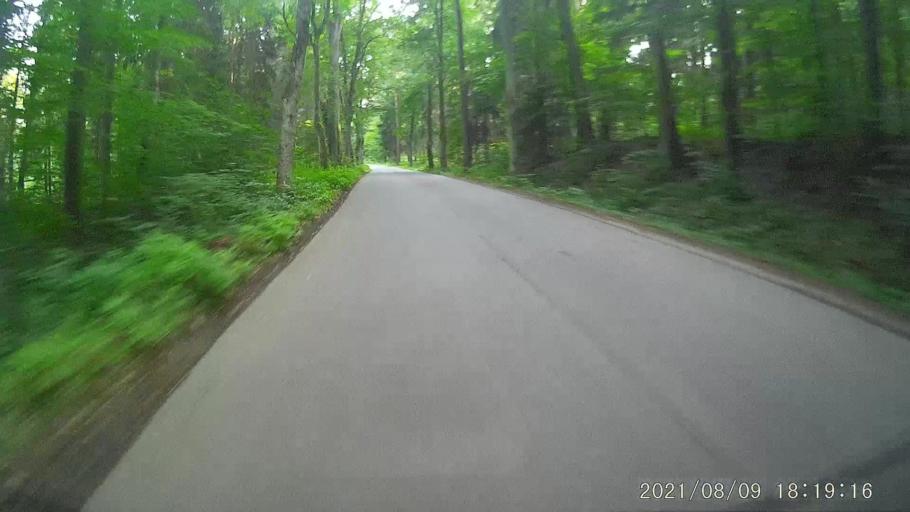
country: PL
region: Lower Silesian Voivodeship
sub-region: Powiat zabkowicki
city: Bardo
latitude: 50.5107
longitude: 16.6835
